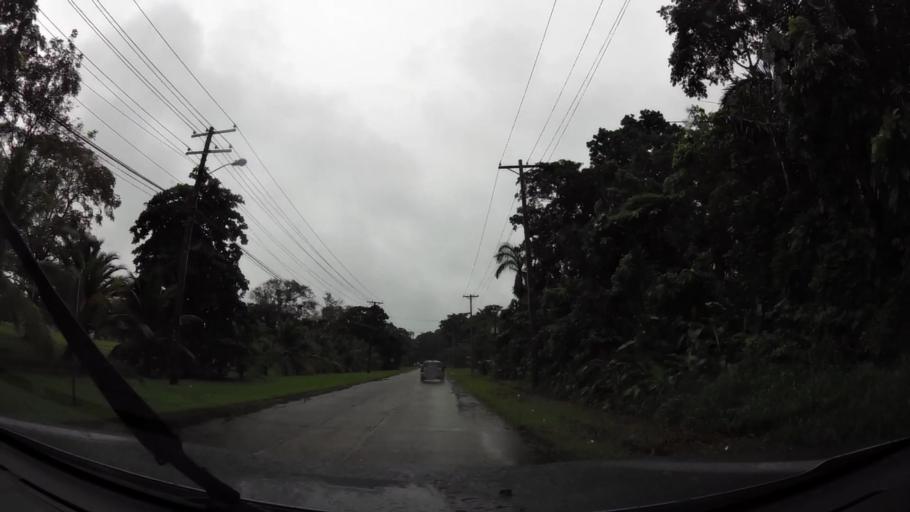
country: PA
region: Colon
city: Las Margaritas
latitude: 9.3237
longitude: -79.8919
